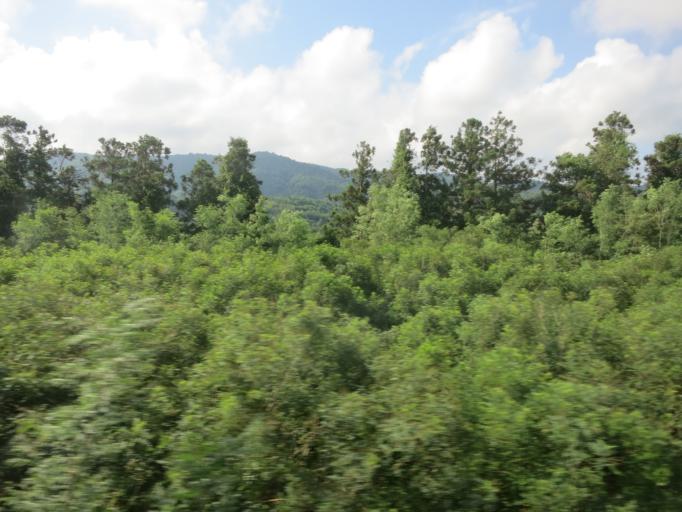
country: GE
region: Guria
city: Lanchkhuti
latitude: 42.0869
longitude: 42.1000
